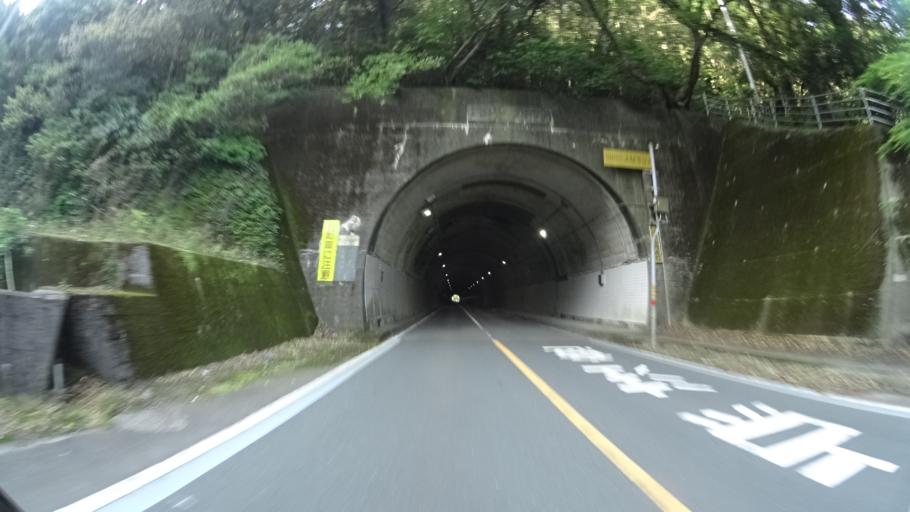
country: JP
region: Ehime
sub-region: Nishiuwa-gun
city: Ikata-cho
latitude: 33.3941
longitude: 132.1374
